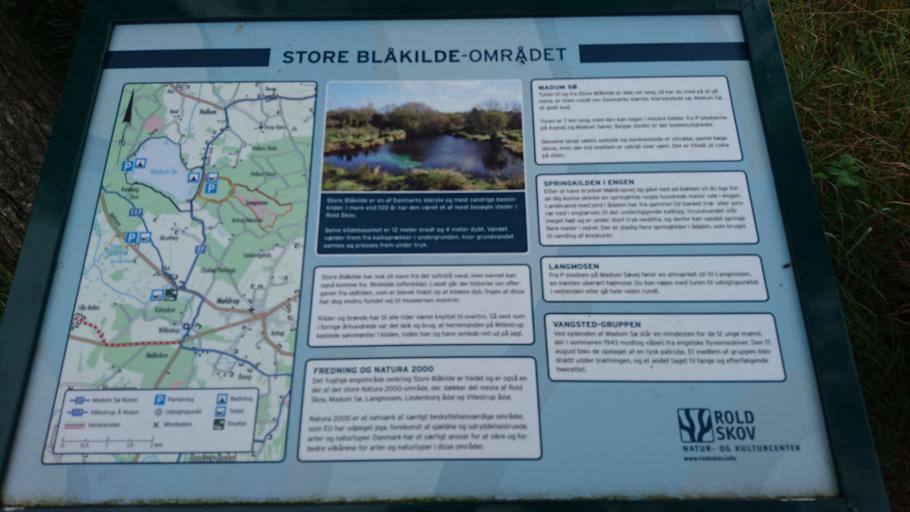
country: DK
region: North Denmark
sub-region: Rebild Kommune
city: Skorping
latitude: 56.7840
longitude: 9.9252
